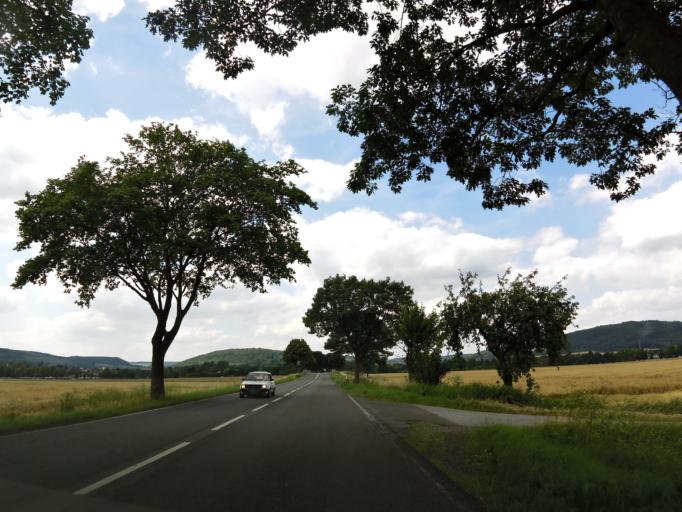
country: DE
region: North Rhine-Westphalia
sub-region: Regierungsbezirk Detmold
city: Hoexter
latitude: 51.7661
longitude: 9.3960
